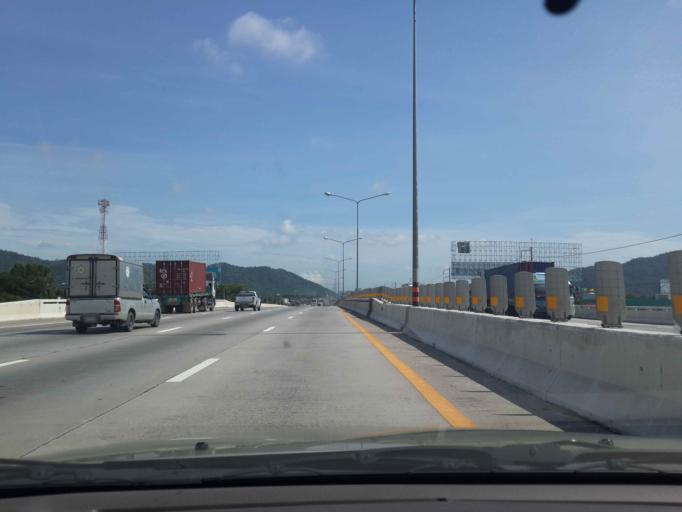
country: TH
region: Chon Buri
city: Si Racha
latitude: 13.2300
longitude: 101.0010
